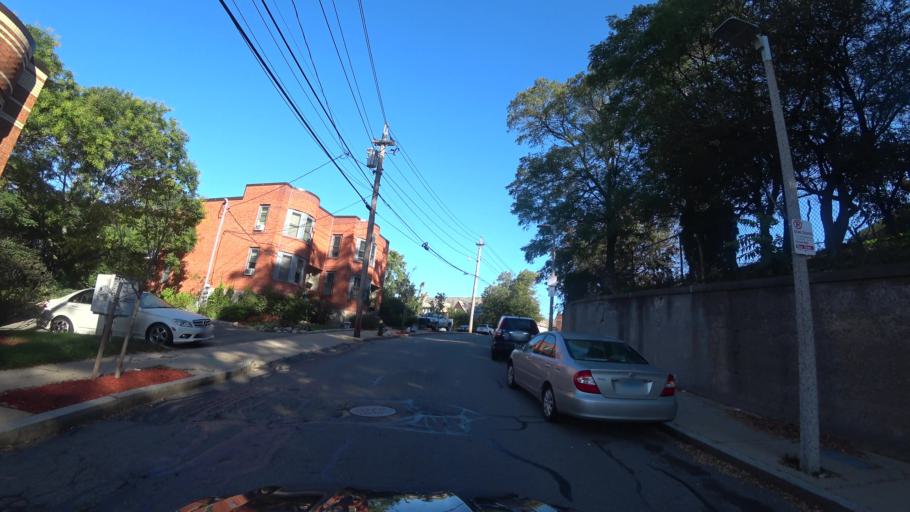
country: US
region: Massachusetts
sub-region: Norfolk County
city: Brookline
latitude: 42.3294
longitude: -71.1087
